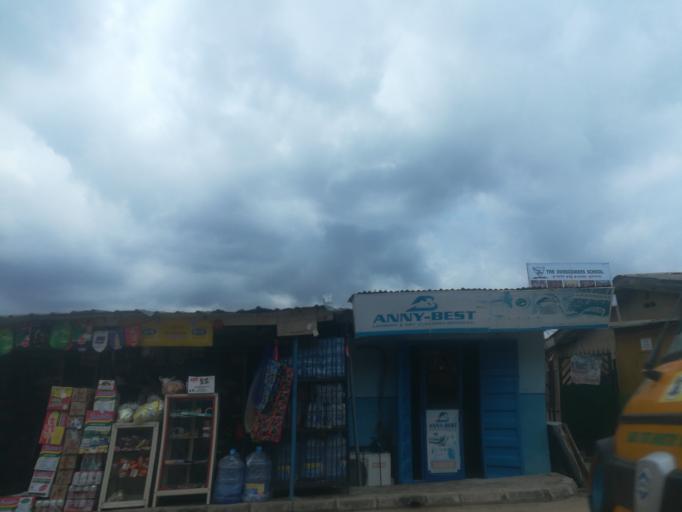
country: NG
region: Lagos
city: Ojota
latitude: 6.5651
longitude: 3.3896
